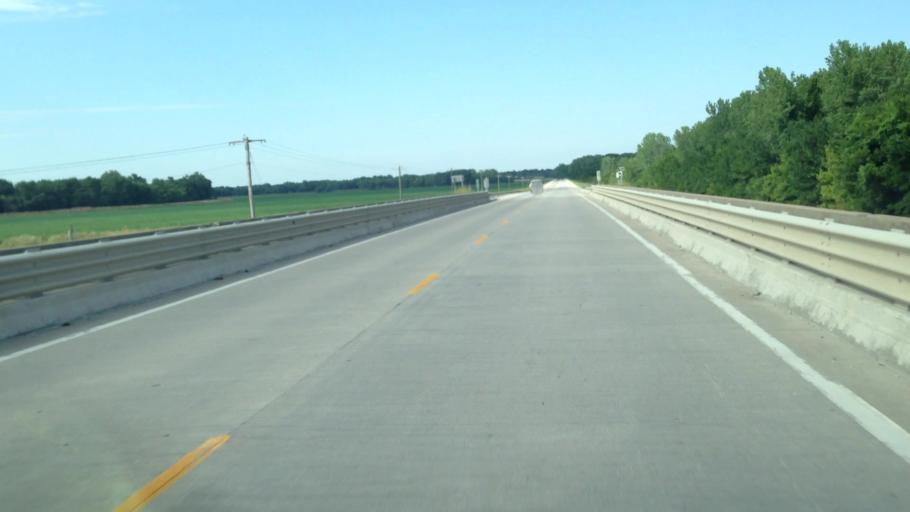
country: US
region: Kansas
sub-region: Neosho County
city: Erie
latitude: 37.5498
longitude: -95.2641
